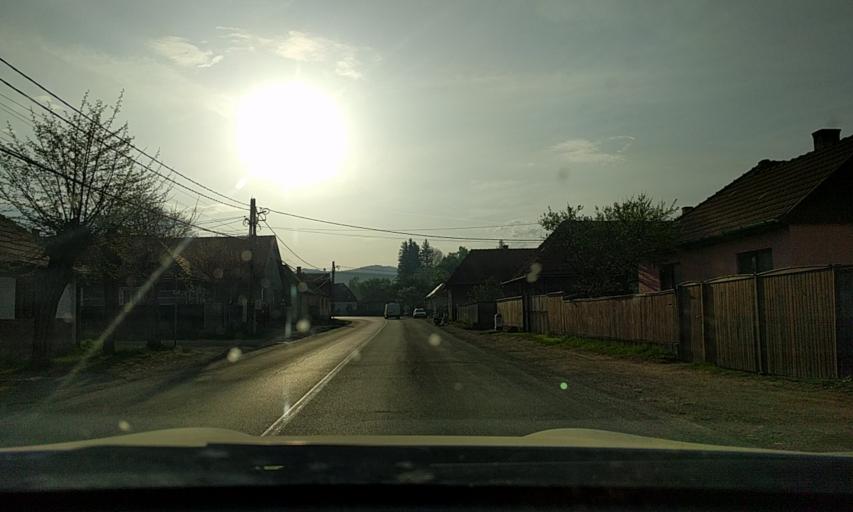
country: RO
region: Covasna
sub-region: Comuna Bretcu
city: Bretcu
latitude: 46.0411
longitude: 26.2948
